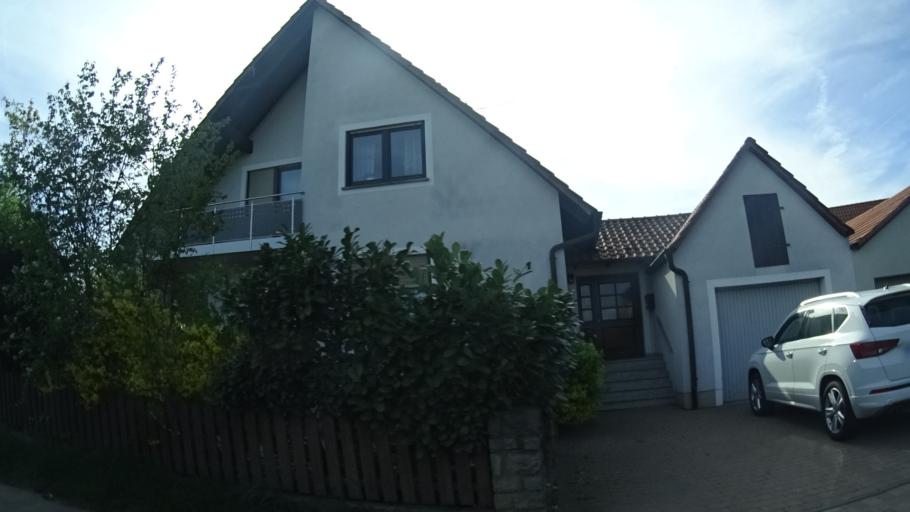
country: DE
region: Bavaria
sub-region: Regierungsbezirk Unterfranken
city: Volkach
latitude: 49.8880
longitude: 10.2277
